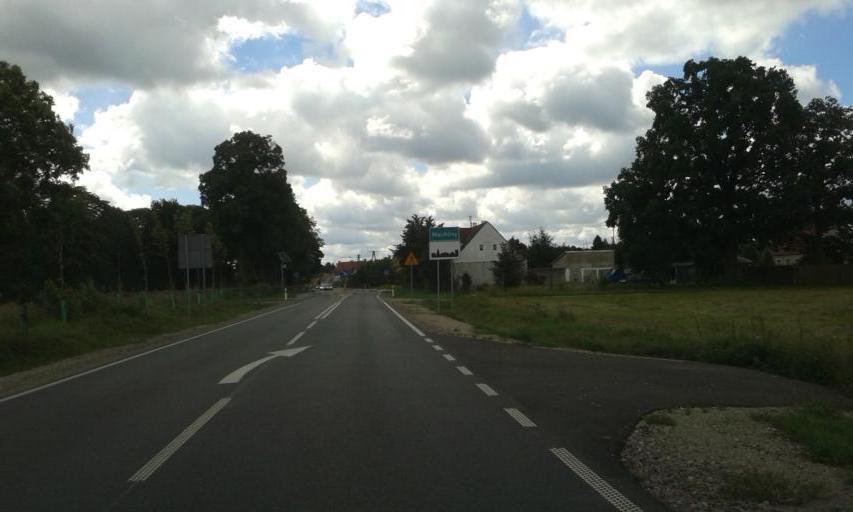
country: PL
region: West Pomeranian Voivodeship
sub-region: Powiat szczecinecki
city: Lubowo
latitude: 53.4858
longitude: 16.3422
